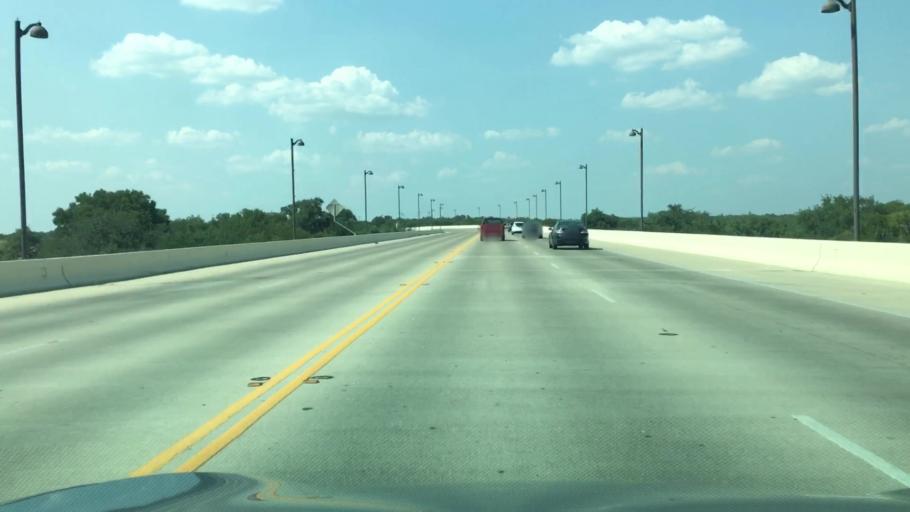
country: US
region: Texas
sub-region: Hays County
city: San Marcos
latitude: 29.8703
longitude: -97.9660
